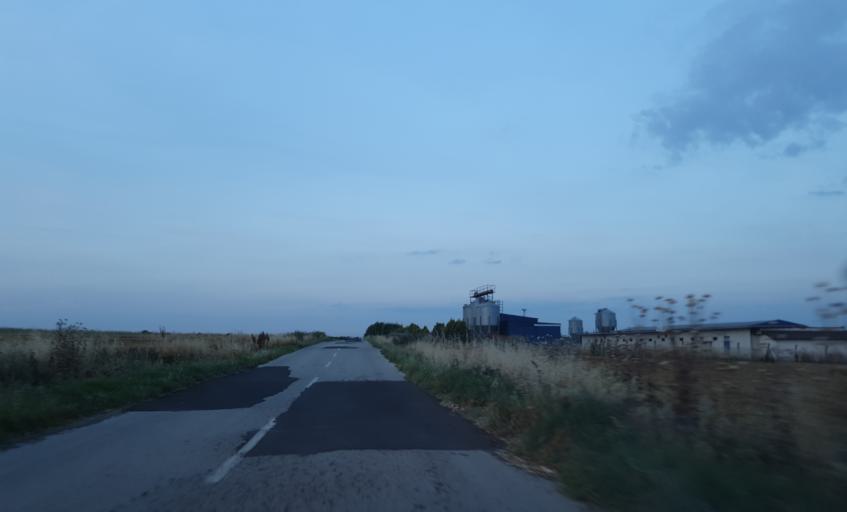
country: TR
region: Tekirdag
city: Beyazkoy
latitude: 41.4301
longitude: 27.6856
